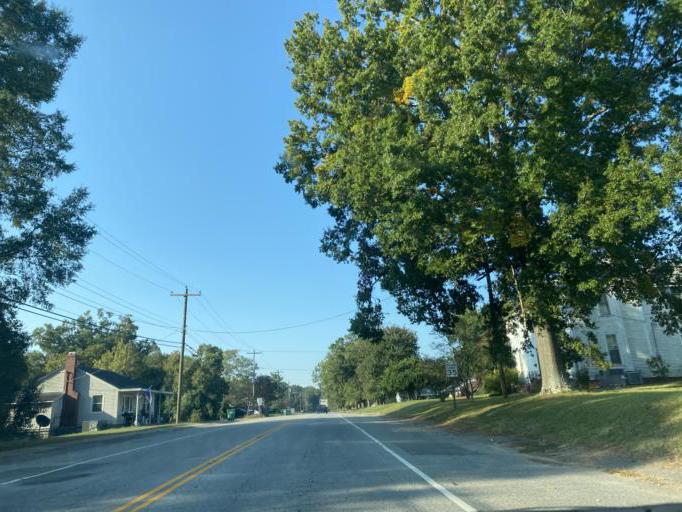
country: US
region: South Carolina
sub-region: Cherokee County
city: Gaffney
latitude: 35.0591
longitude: -81.6605
